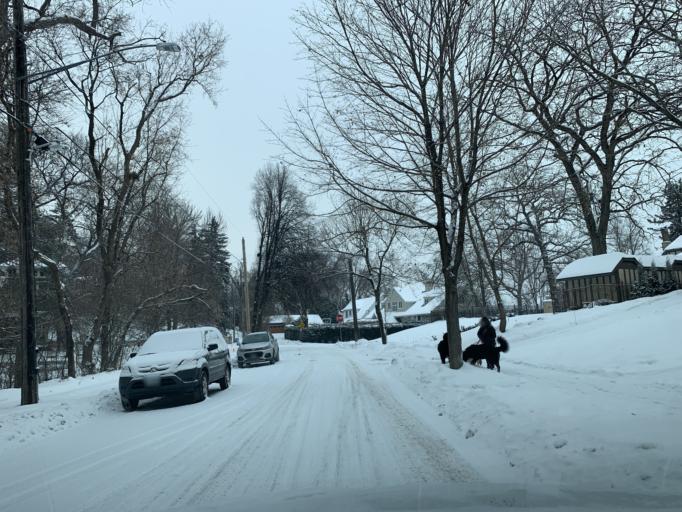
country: US
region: Minnesota
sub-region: Hennepin County
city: Saint Louis Park
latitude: 44.9397
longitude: -93.3215
